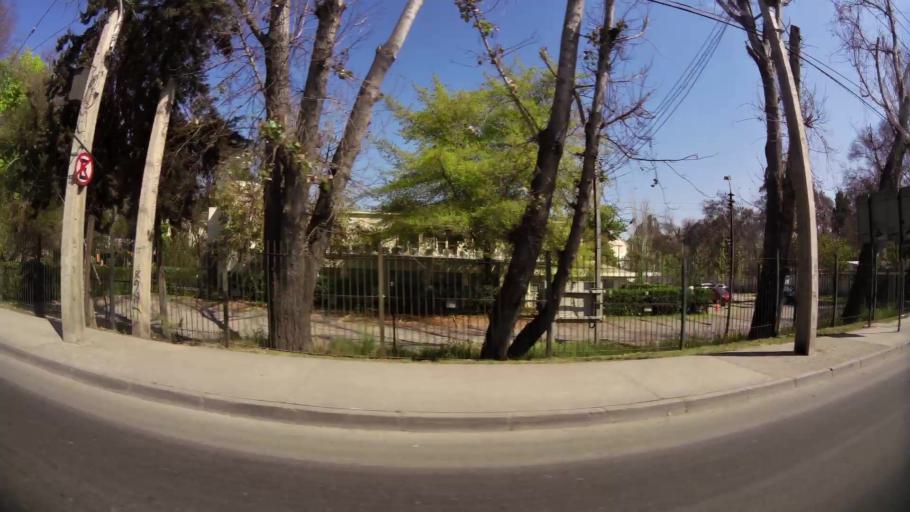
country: CL
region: Santiago Metropolitan
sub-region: Provincia de Santiago
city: Santiago
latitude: -33.4670
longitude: -70.6568
